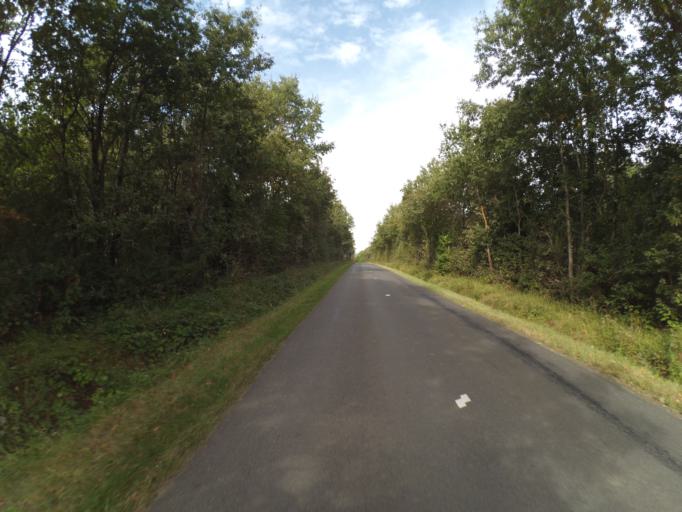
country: FR
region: Pays de la Loire
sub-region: Departement de Maine-et-Loire
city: Saint-Jean
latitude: 47.1930
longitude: -0.3521
